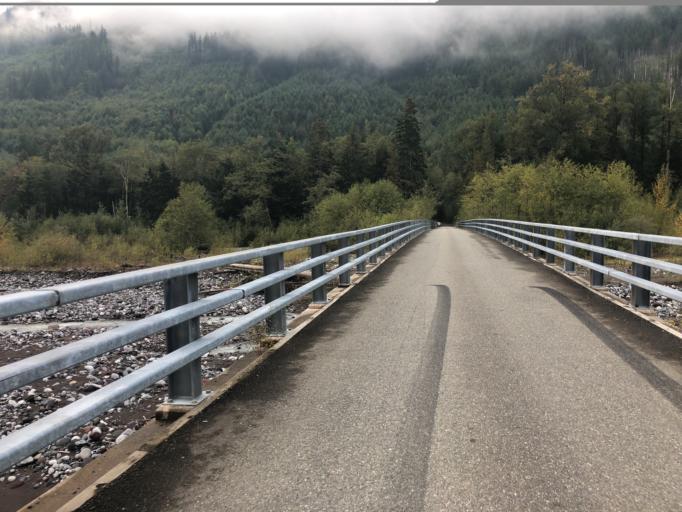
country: US
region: Washington
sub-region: Pierce County
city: Buckley
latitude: 46.9955
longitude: -121.9201
